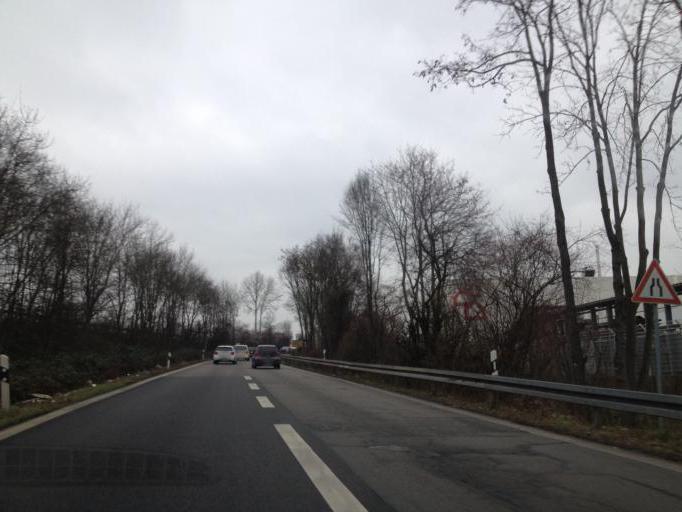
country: DE
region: Rheinland-Pfalz
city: Altrip
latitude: 49.4546
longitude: 8.5116
